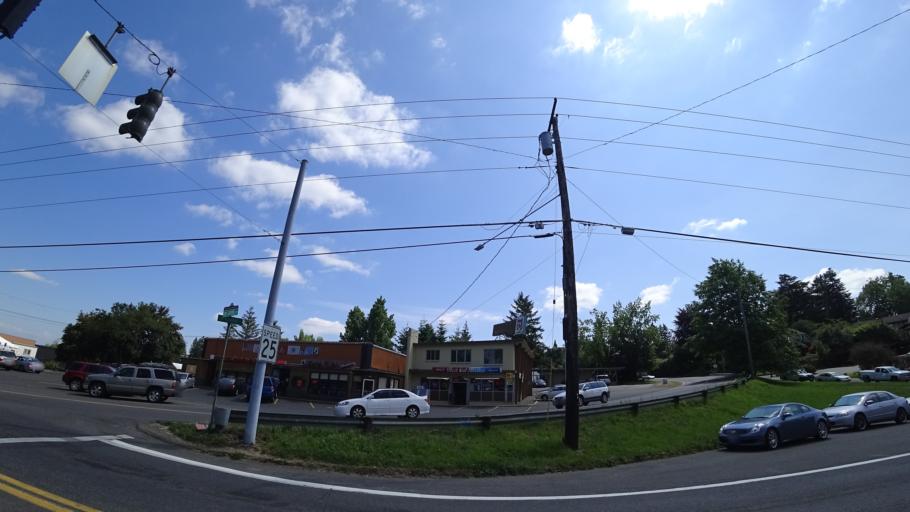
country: US
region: Oregon
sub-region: Washington County
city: Garden Home-Whitford
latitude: 45.4761
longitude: -122.7070
